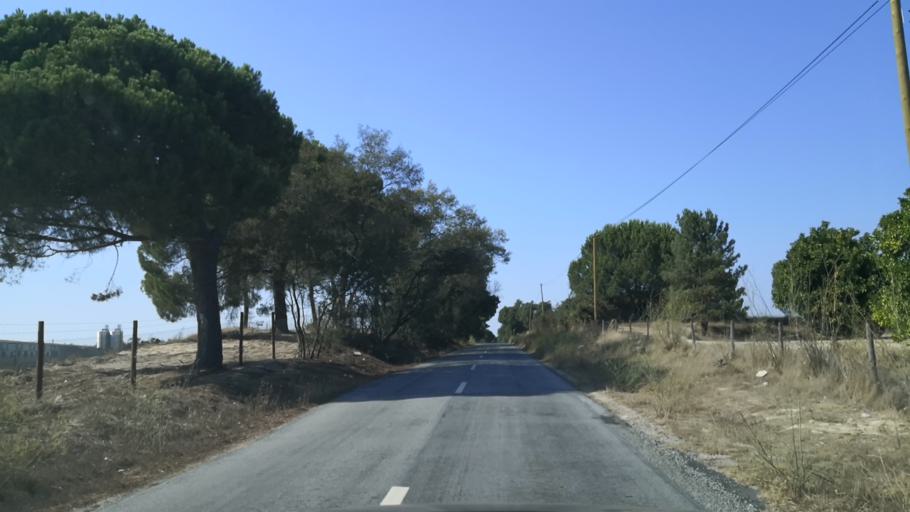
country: PT
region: Evora
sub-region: Vendas Novas
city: Vendas Novas
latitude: 38.7209
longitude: -8.6194
